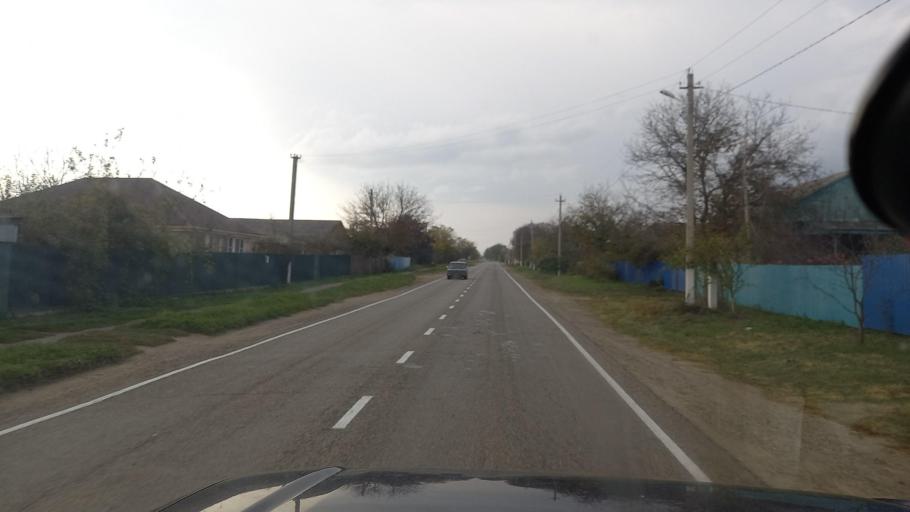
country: RU
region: Krasnodarskiy
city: Gubskaya
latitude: 44.3177
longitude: 40.6234
